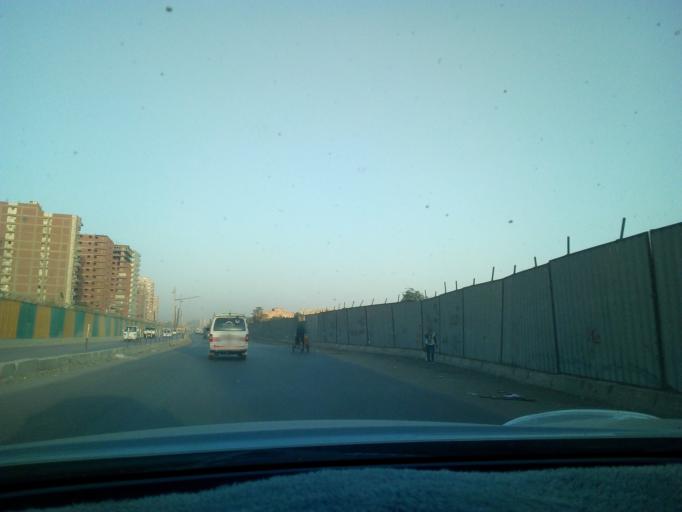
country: EG
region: Muhafazat al Qalyubiyah
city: Al Khankah
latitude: 30.1264
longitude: 31.3523
